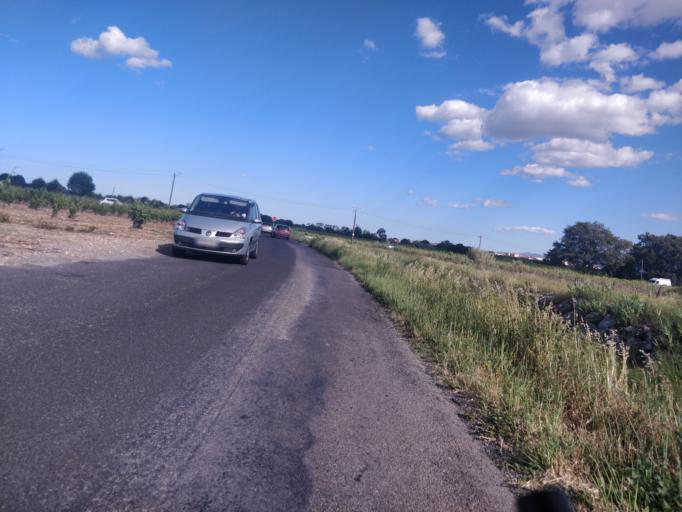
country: FR
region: Languedoc-Roussillon
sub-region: Departement des Pyrenees-Orientales
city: Cabestany
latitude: 42.6689
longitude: 2.9302
